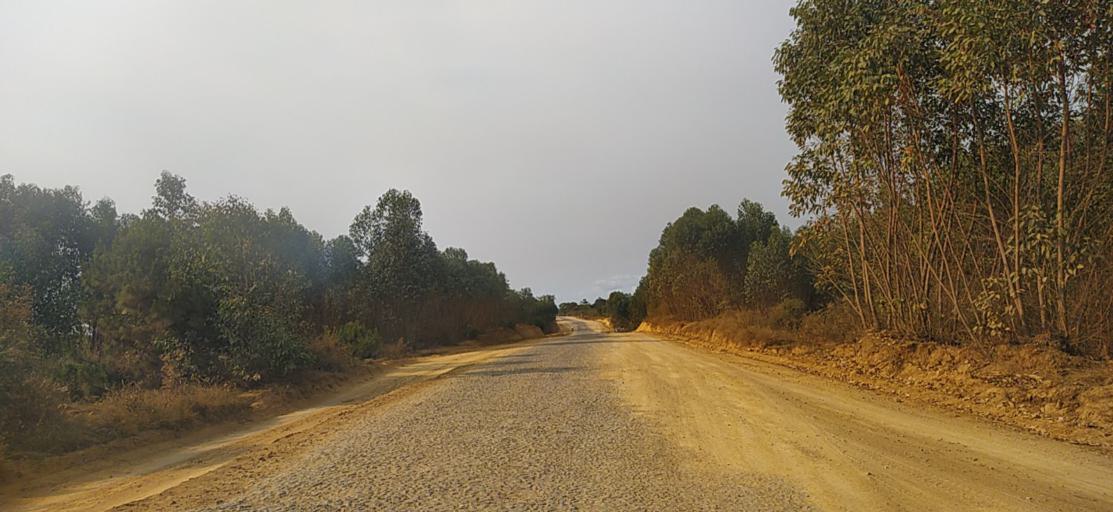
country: MG
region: Alaotra Mangoro
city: Moramanga
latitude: -18.6417
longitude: 48.2755
